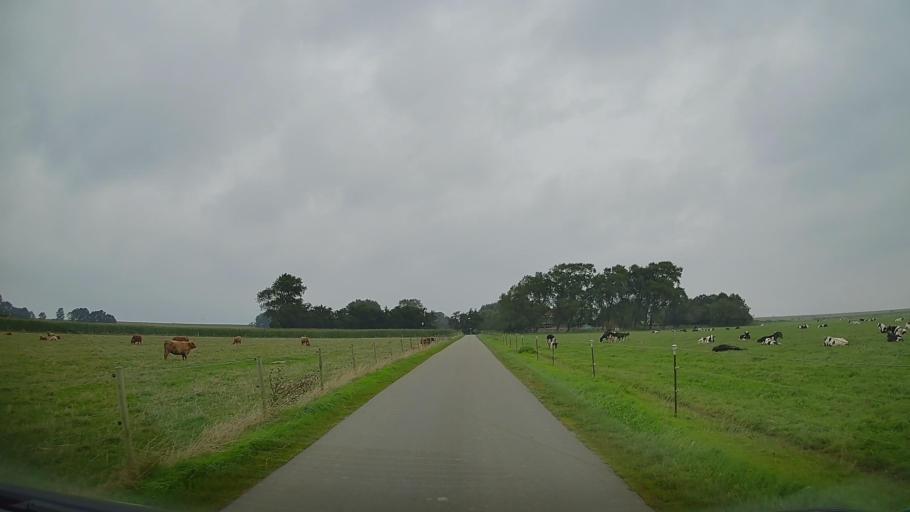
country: DE
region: Lower Saxony
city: Otterndorf
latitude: 53.8196
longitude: 8.9207
